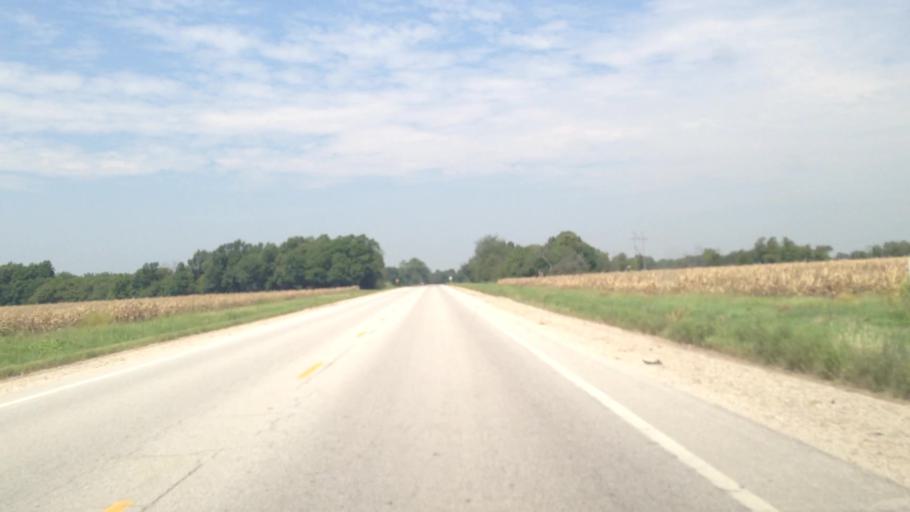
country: US
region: Kansas
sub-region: Labette County
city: Parsons
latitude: 37.3861
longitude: -95.2649
